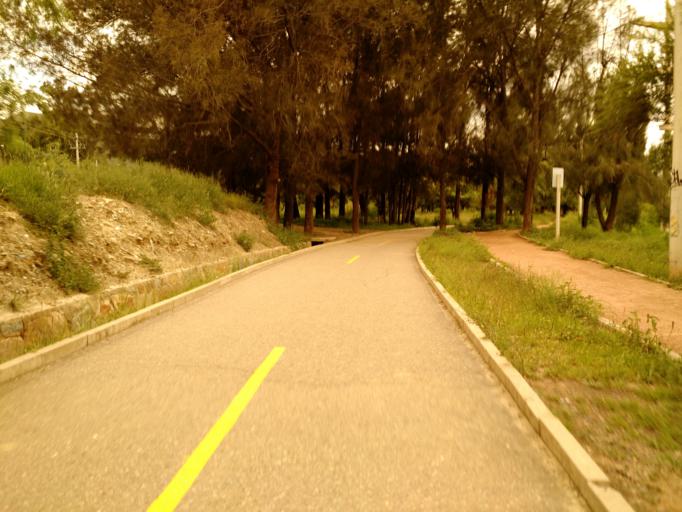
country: BO
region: Cochabamba
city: Cochabamba
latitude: -17.4016
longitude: -66.1333
